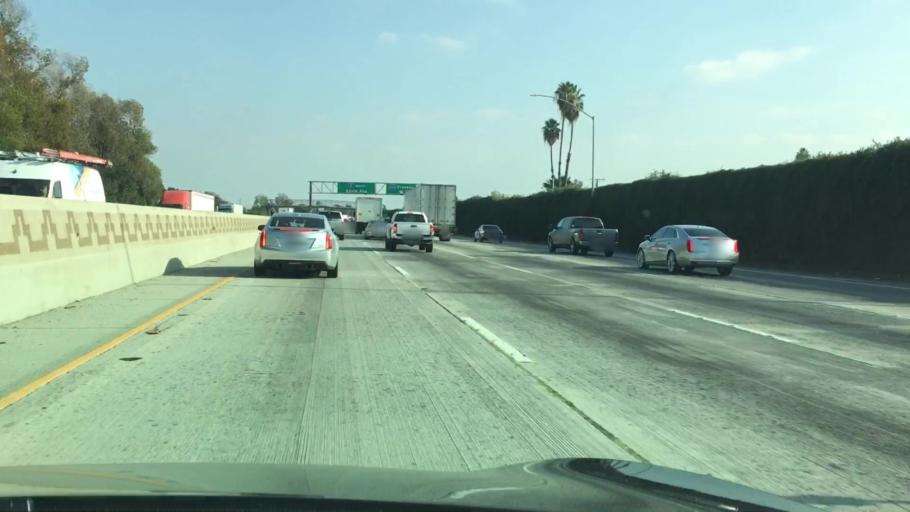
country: US
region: California
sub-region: Los Angeles County
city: Santa Fe Springs
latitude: 33.9556
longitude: -118.1087
